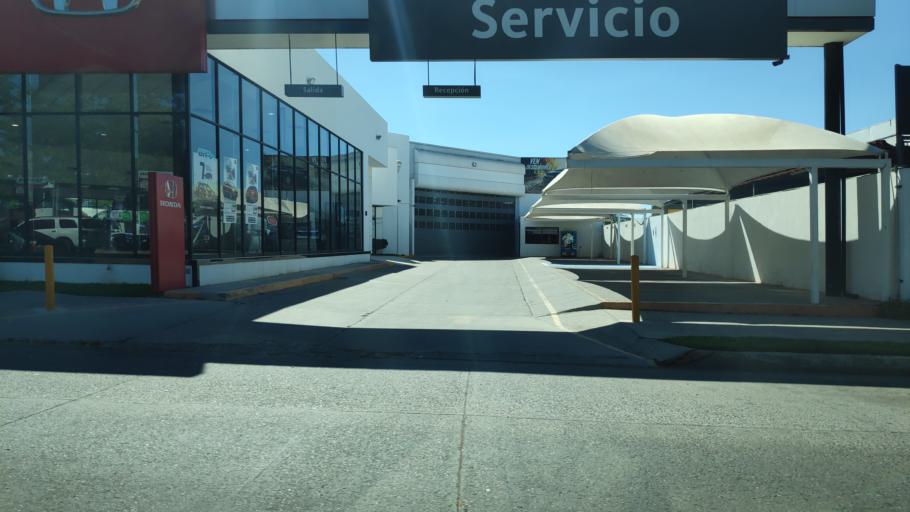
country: MX
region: Sinaloa
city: Culiacan
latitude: 24.8203
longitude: -107.4010
